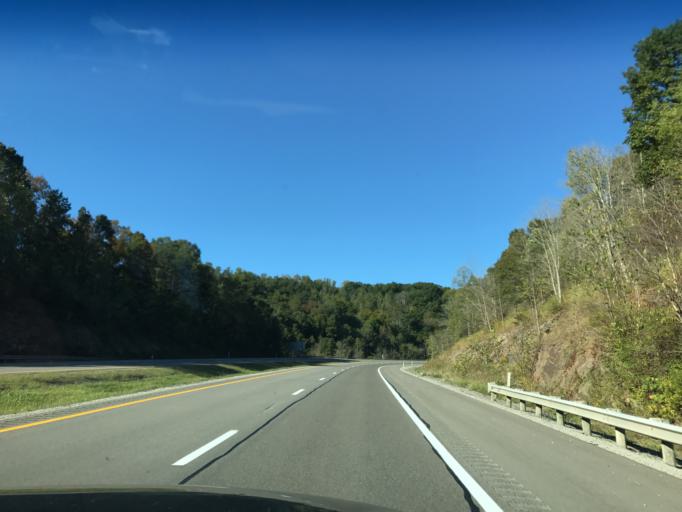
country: US
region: Ohio
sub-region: Washington County
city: Reno
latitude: 39.2418
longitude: -81.4016
